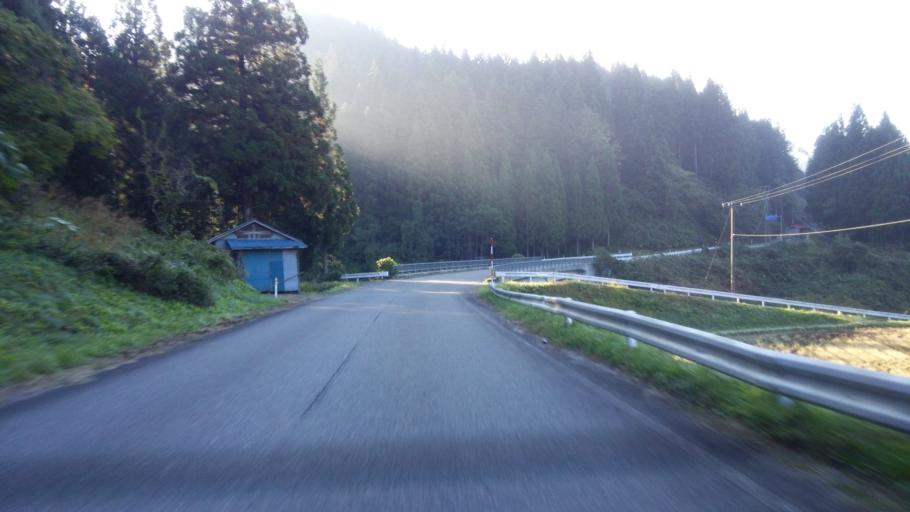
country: JP
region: Fukushima
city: Kitakata
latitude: 37.4293
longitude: 139.7260
